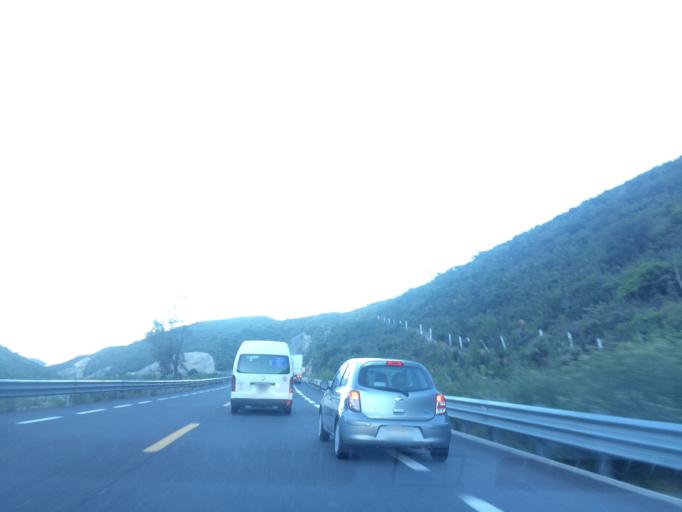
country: MX
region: Puebla
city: Chapuco
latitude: 18.6461
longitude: -97.4548
